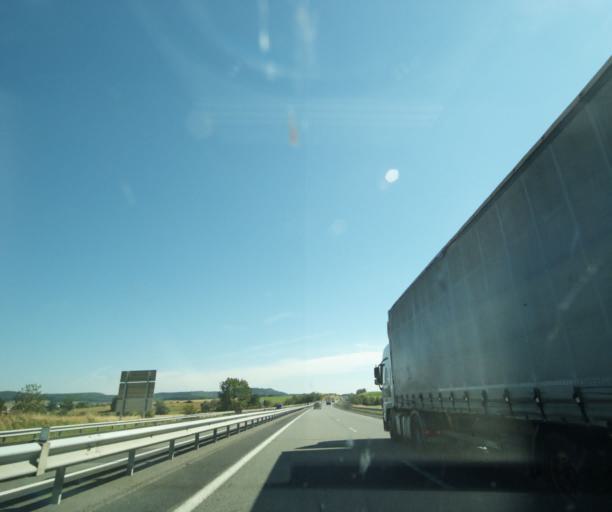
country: FR
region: Lorraine
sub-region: Departement des Vosges
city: Lamarche
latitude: 48.1583
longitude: 5.6995
